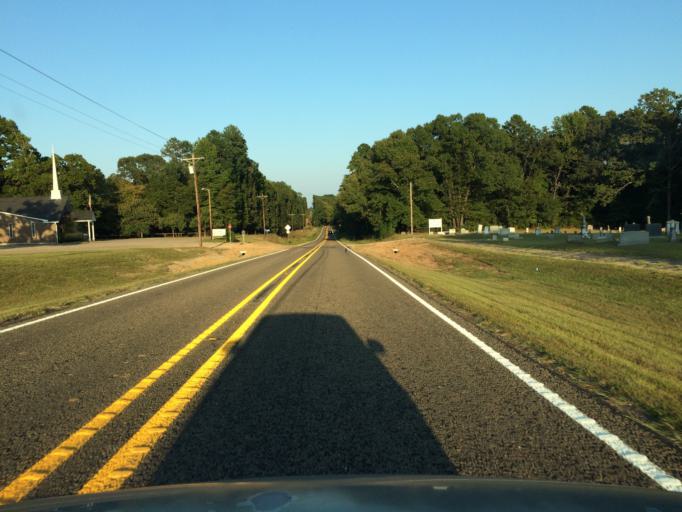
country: US
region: Texas
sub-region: Wood County
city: Quitman
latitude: 32.7375
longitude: -95.3137
